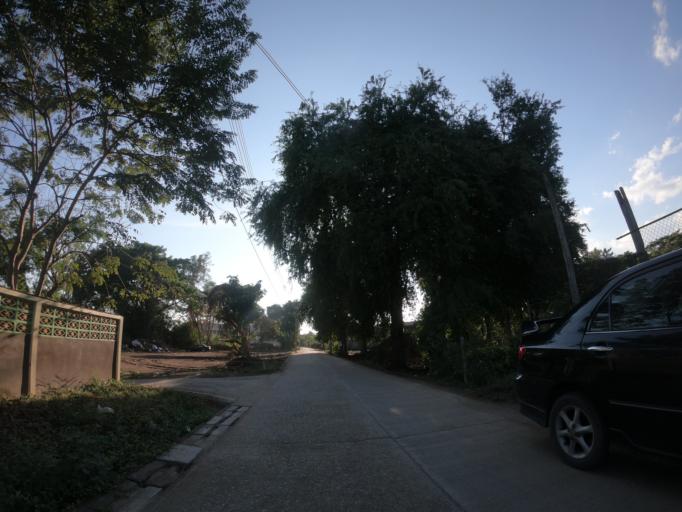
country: TH
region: Chiang Mai
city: Chiang Mai
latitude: 18.7442
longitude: 98.9824
